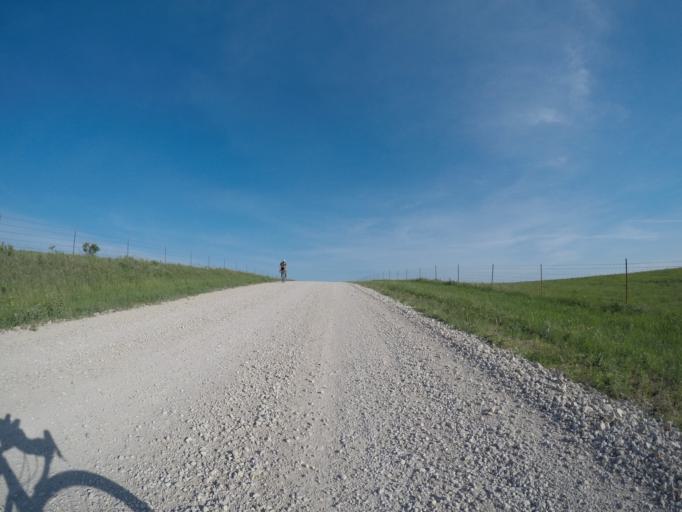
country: US
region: Kansas
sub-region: Riley County
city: Manhattan
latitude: 39.0402
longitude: -96.4911
